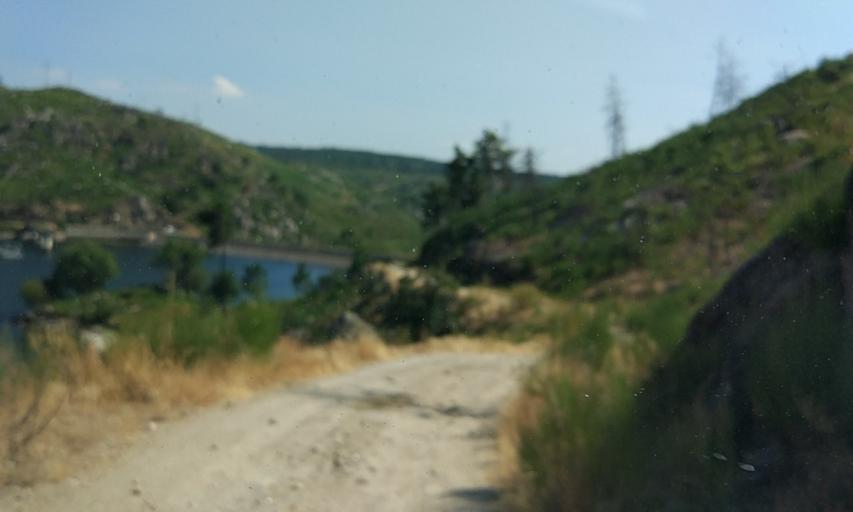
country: PT
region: Vila Real
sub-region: Sabrosa
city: Sabrosa
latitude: 41.3119
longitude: -7.4916
